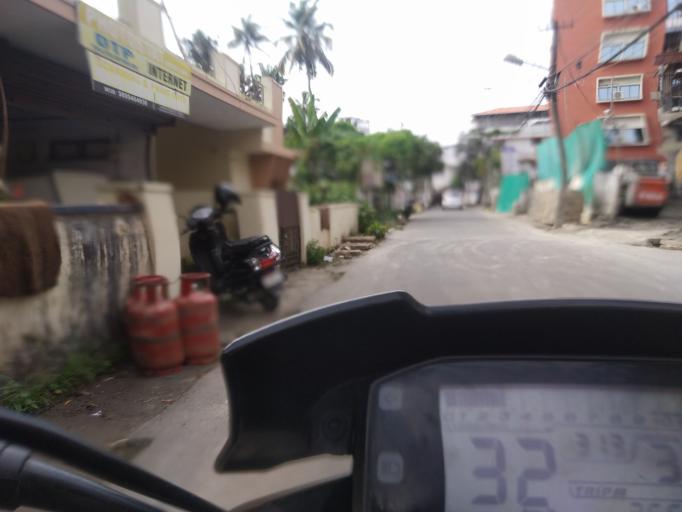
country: IN
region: Kerala
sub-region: Ernakulam
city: Cochin
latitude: 9.9712
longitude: 76.2884
